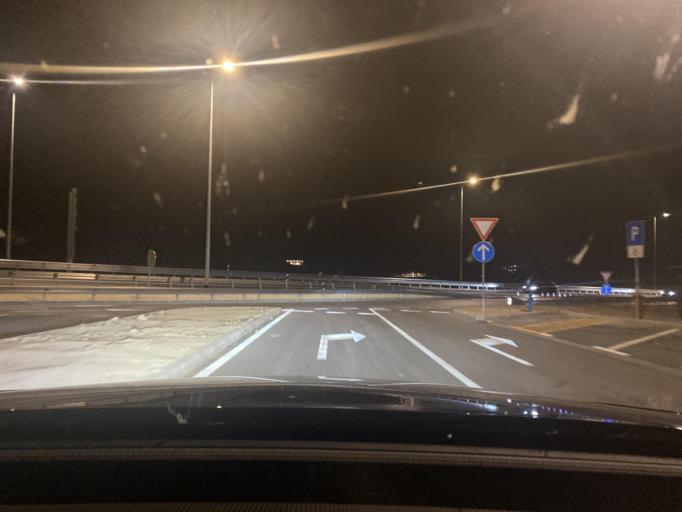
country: HR
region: Dubrovacko-Neretvanska
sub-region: Grad Dubrovnik
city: Opuzen
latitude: 42.9431
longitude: 17.5417
